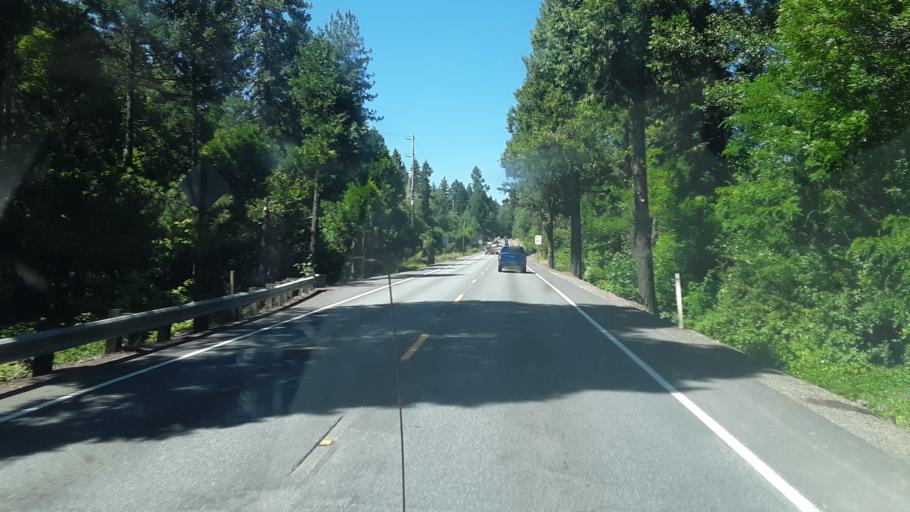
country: US
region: Oregon
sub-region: Josephine County
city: Cave Junction
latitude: 42.2920
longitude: -123.6124
